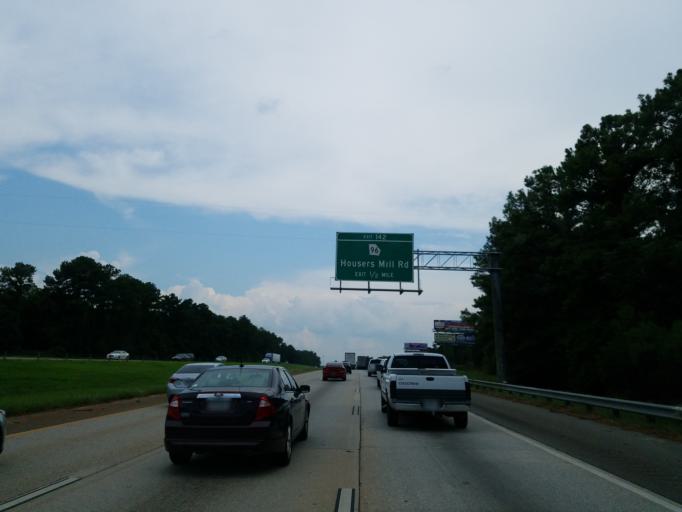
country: US
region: Georgia
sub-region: Houston County
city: Centerville
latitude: 32.5611
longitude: -83.7444
